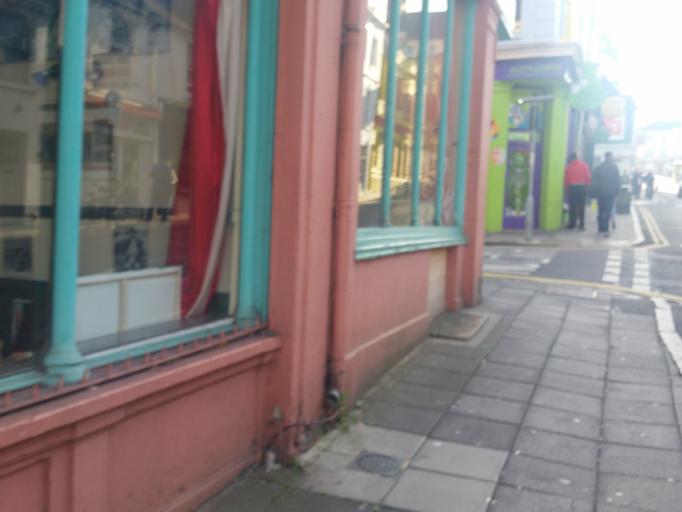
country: GB
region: England
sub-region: Brighton and Hove
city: Brighton
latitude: 50.8257
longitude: -0.1396
